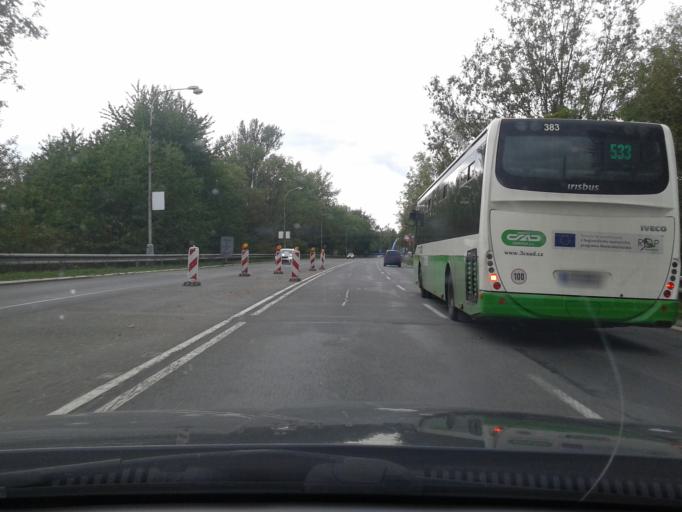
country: CZ
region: Moravskoslezsky
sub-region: Okres Karvina
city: Karvina
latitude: 49.8515
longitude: 18.5279
